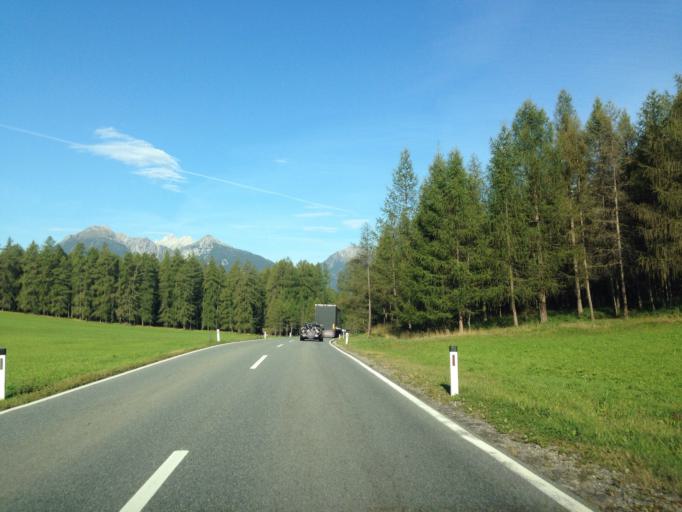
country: AT
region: Tyrol
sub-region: Politischer Bezirk Imst
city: Obsteig
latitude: 47.3055
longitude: 10.8923
